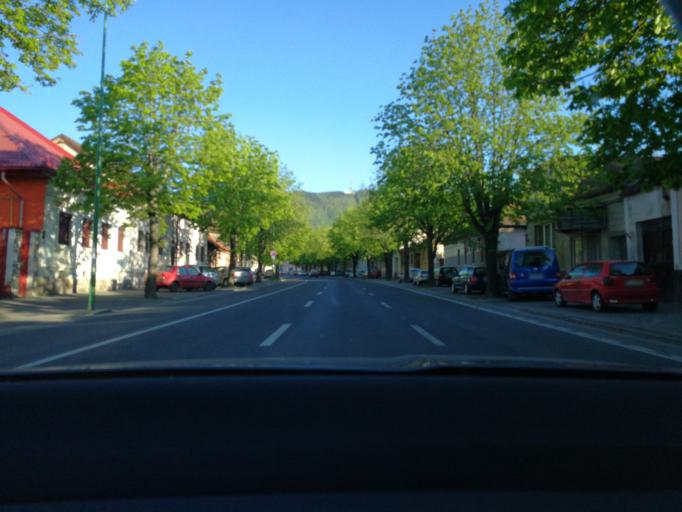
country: RO
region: Brasov
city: Brasov
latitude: 45.6541
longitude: 25.5836
